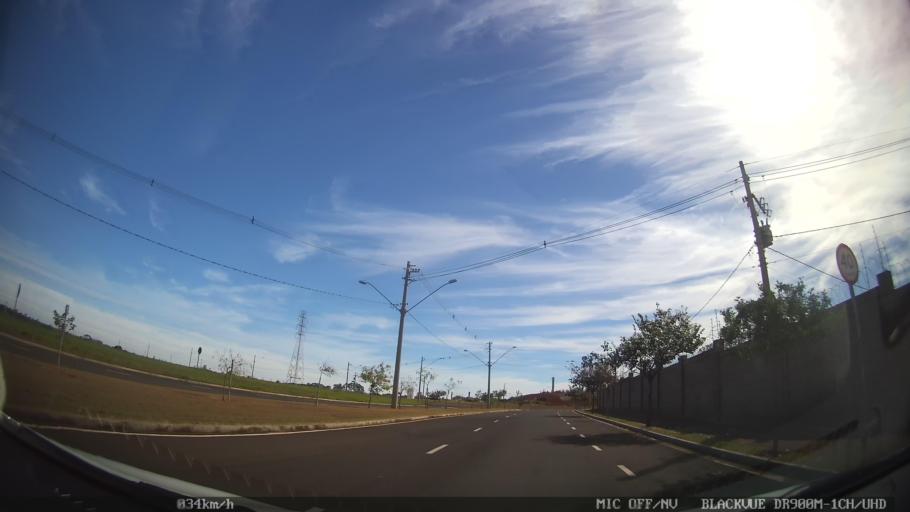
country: BR
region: Sao Paulo
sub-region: Sao Jose Do Rio Preto
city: Sao Jose do Rio Preto
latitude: -20.8513
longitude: -49.3745
